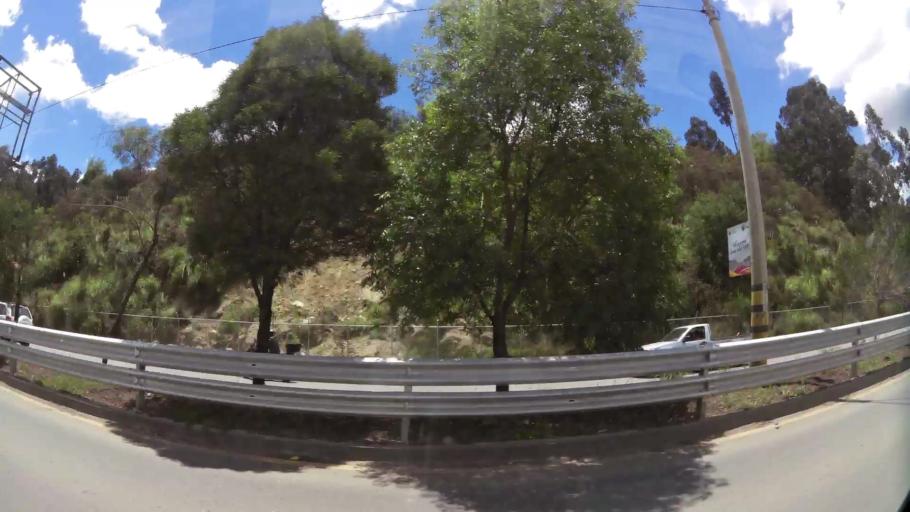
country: EC
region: Azuay
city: Cuenca
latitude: -2.8987
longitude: -78.9681
